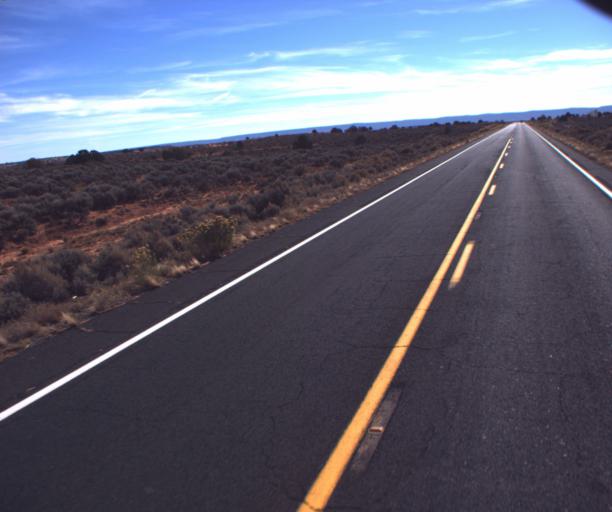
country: US
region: Arizona
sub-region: Coconino County
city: Kaibito
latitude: 36.5704
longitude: -110.7642
